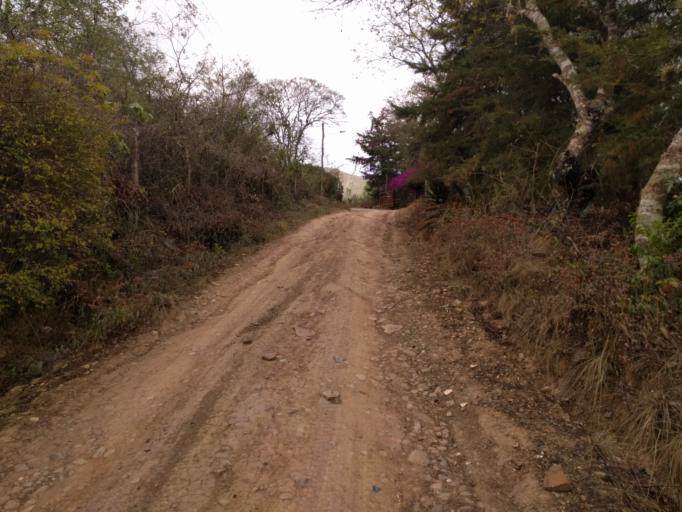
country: BO
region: Santa Cruz
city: Samaipata
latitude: -18.1882
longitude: -63.8790
